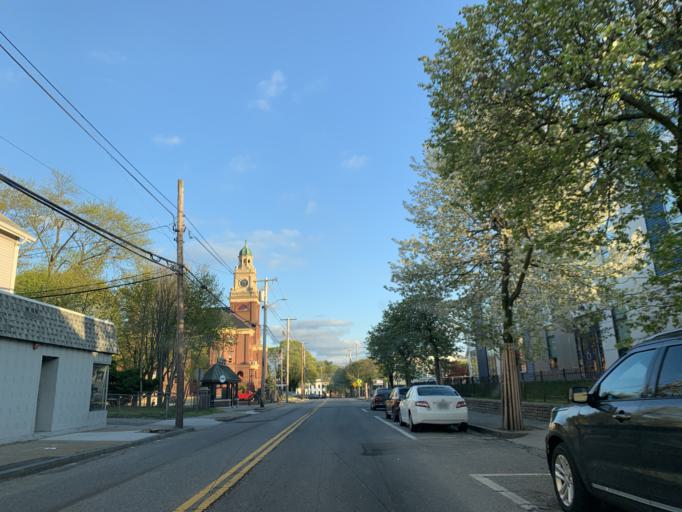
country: US
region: Rhode Island
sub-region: Providence County
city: Valley Falls
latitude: 41.9016
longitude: -71.3913
